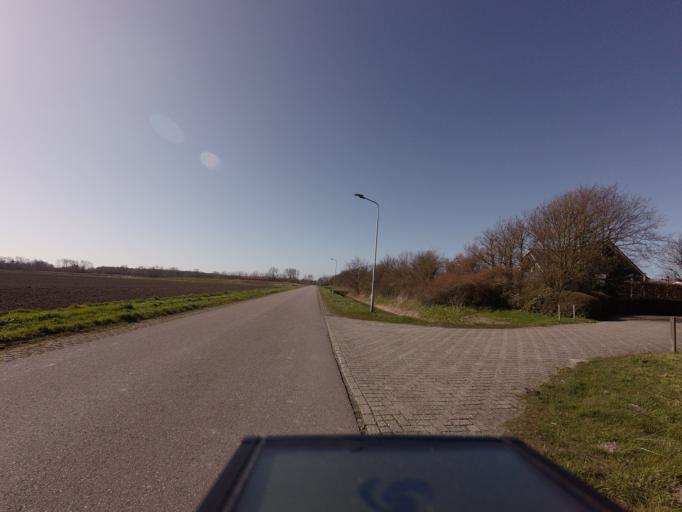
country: NL
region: Zeeland
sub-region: Schouwen-Duiveland
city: Renesse
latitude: 51.7361
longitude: 3.7968
